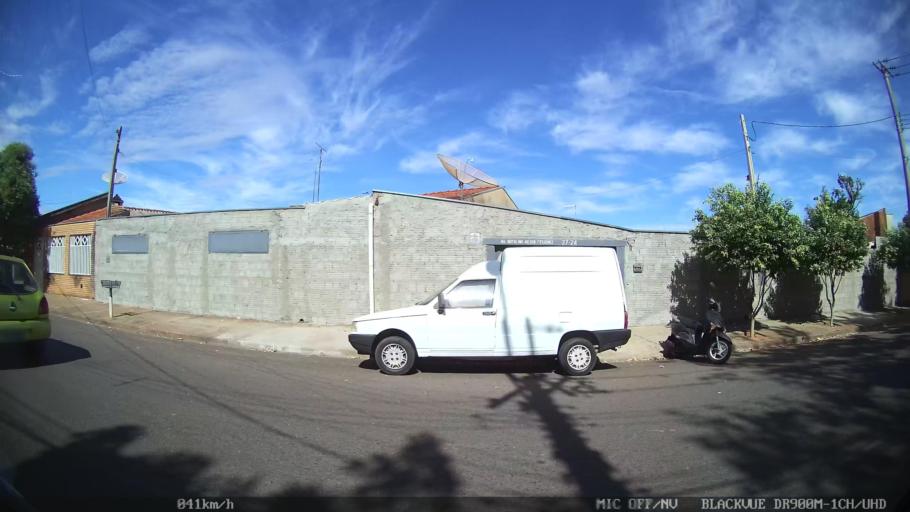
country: BR
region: Sao Paulo
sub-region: Bady Bassitt
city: Bady Bassitt
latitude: -20.8216
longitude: -49.4937
